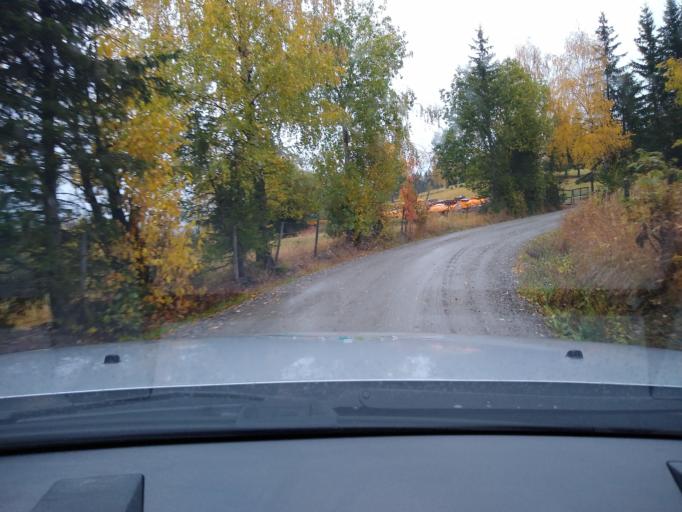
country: NO
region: Oppland
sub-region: Ringebu
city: Ringebu
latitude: 61.5533
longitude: 10.1512
